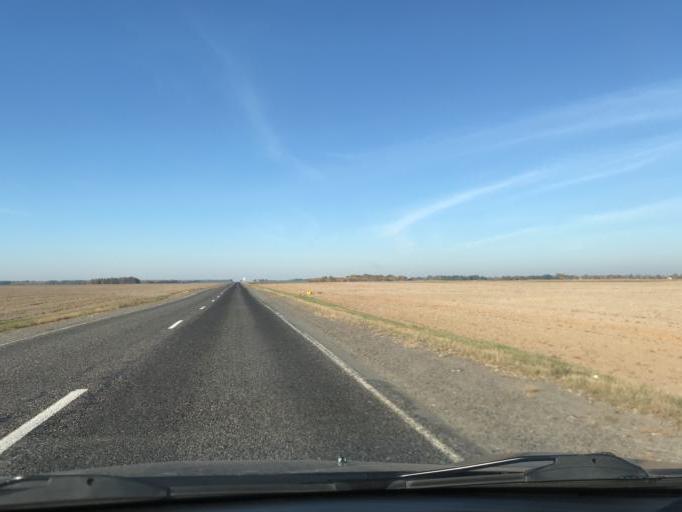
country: BY
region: Gomel
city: Brahin
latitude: 51.7869
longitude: 30.1967
